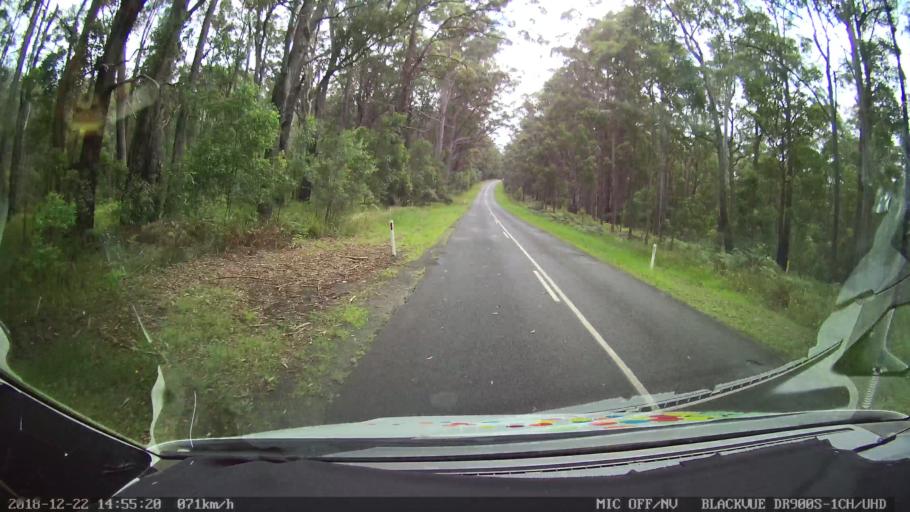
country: AU
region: New South Wales
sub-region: Bellingen
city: Dorrigo
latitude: -30.2292
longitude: 152.5227
